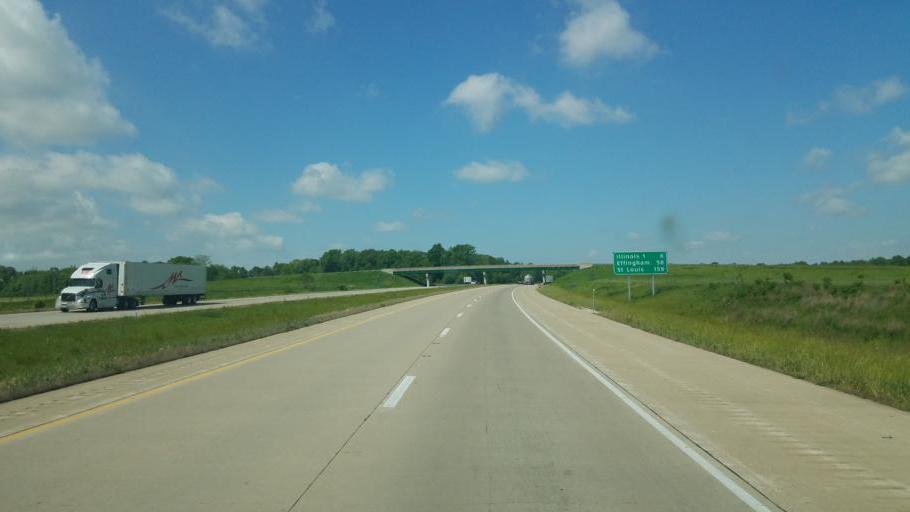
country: US
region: Illinois
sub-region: Clark County
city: Marshall
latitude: 39.4267
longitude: -87.5796
